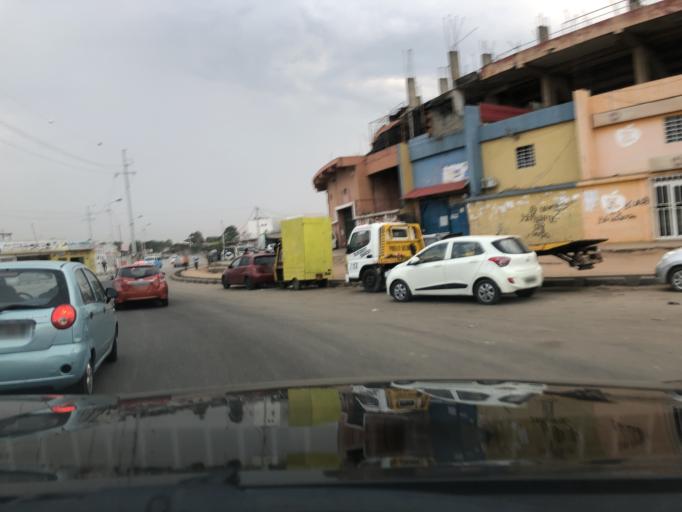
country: AO
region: Luanda
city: Luanda
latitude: -8.8398
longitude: 13.2518
